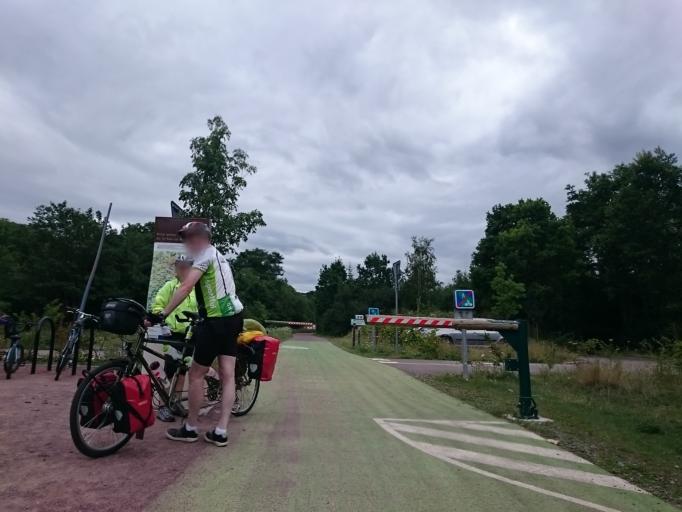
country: FR
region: Lower Normandy
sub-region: Departement du Calvados
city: Saint-Andre-sur-Orne
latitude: 49.1067
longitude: -0.3851
